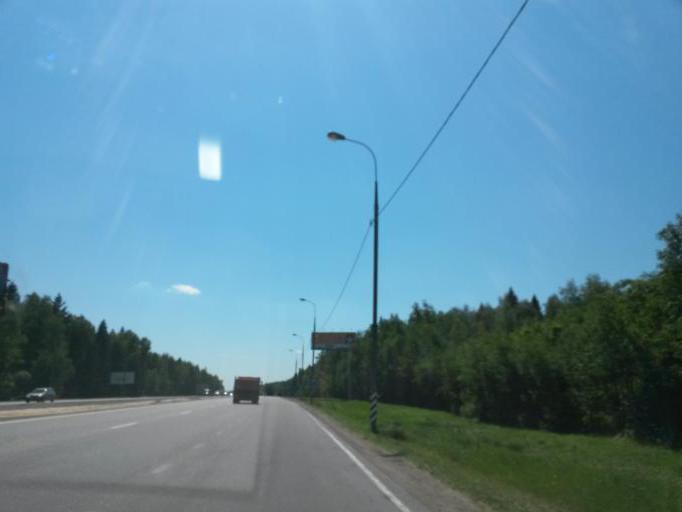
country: RU
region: Moskovskaya
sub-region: Chekhovskiy Rayon
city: Chekhov
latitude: 55.1819
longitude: 37.5352
